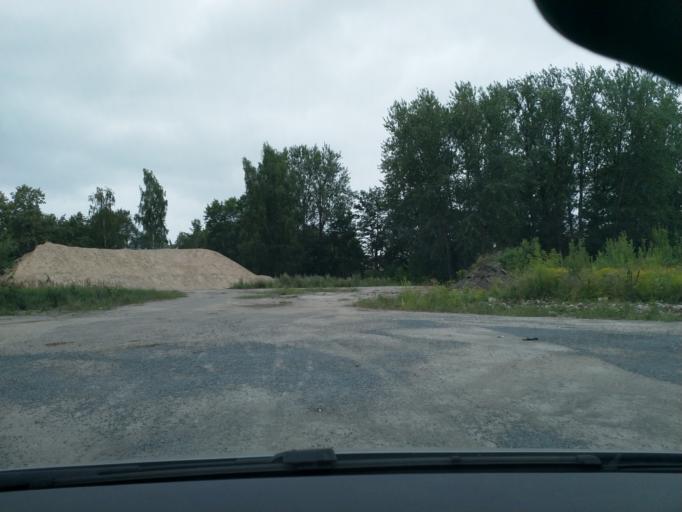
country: LV
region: Kuldigas Rajons
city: Kuldiga
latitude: 56.9656
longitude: 21.9788
